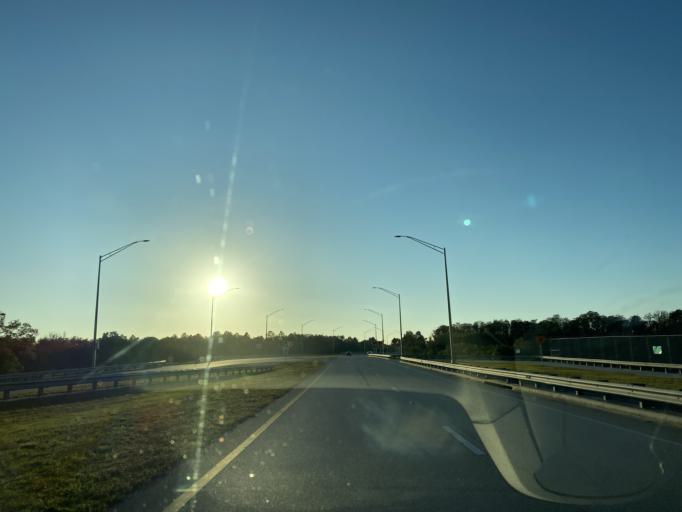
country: US
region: Florida
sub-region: Orange County
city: Meadow Woods
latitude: 28.3978
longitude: -81.3028
